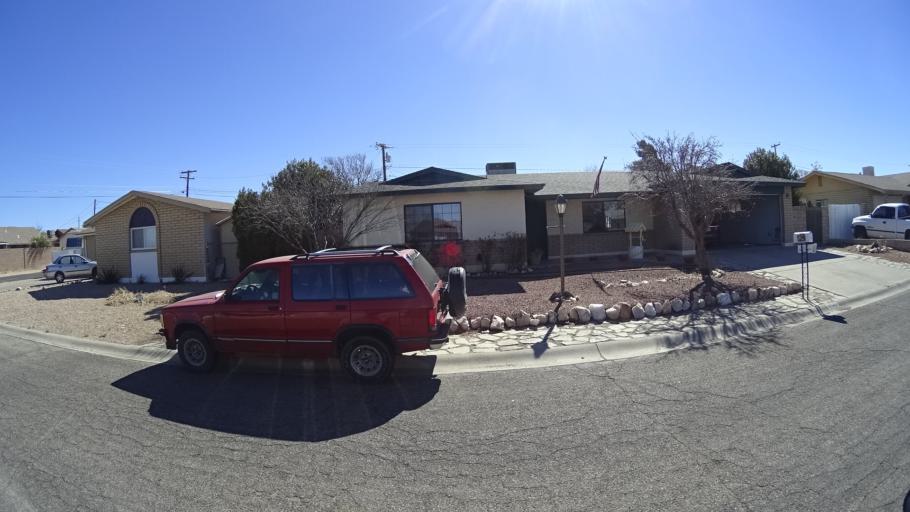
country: US
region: Arizona
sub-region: Mohave County
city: Kingman
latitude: 35.2093
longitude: -114.0218
